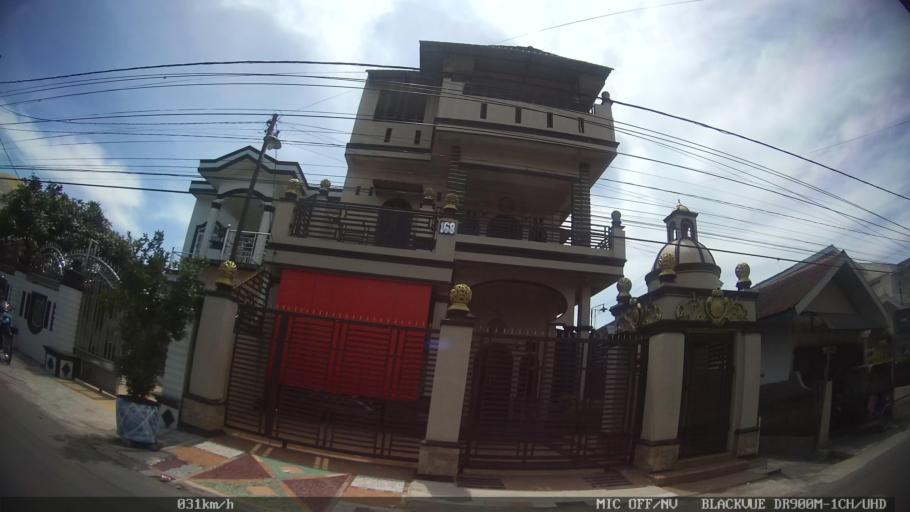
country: ID
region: North Sumatra
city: Binjai
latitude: 3.6071
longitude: 98.4905
